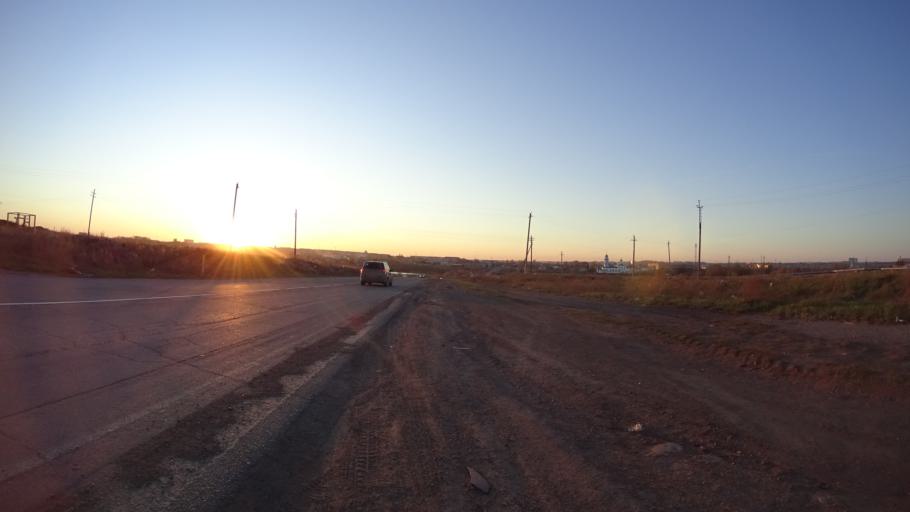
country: RU
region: Chelyabinsk
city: Troitsk
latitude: 54.0714
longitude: 61.5602
